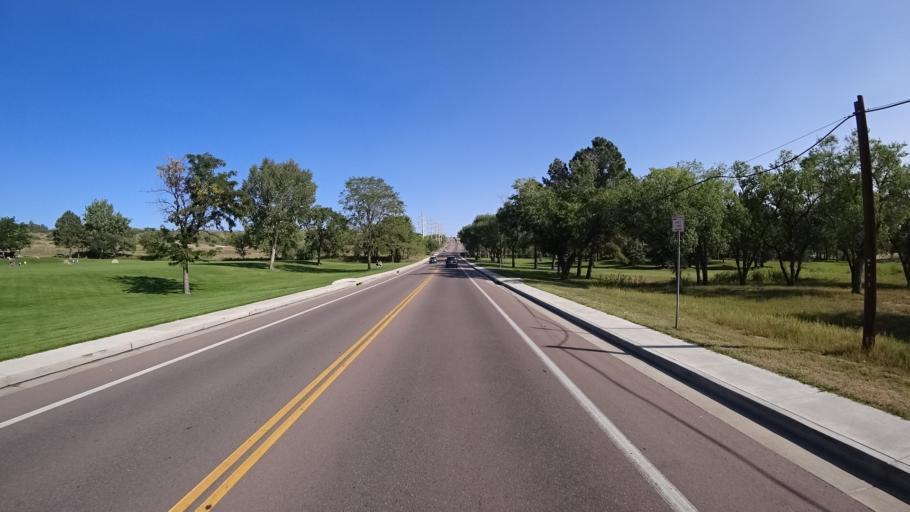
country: US
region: Colorado
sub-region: El Paso County
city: Colorado Springs
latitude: 38.8226
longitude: -104.8593
